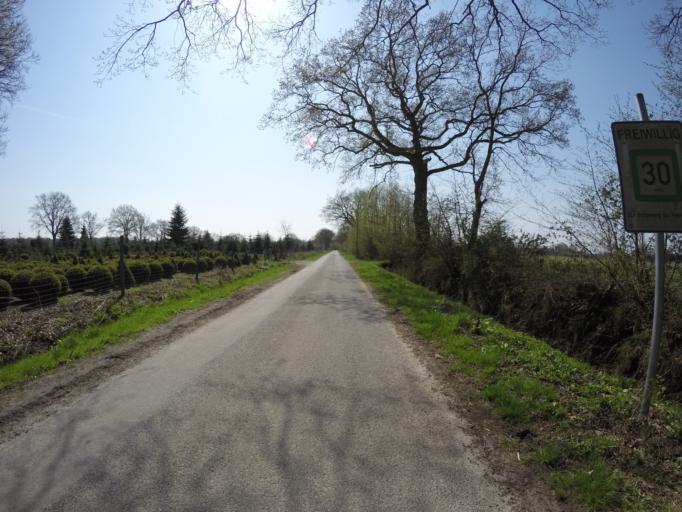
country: DE
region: Schleswig-Holstein
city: Hemdingen
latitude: 53.7587
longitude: 9.8485
